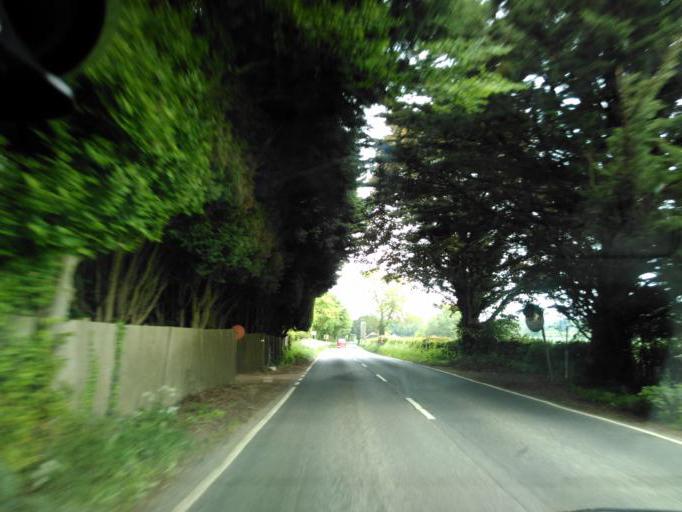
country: GB
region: England
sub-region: Kent
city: Chartham
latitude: 51.1978
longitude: 1.0566
